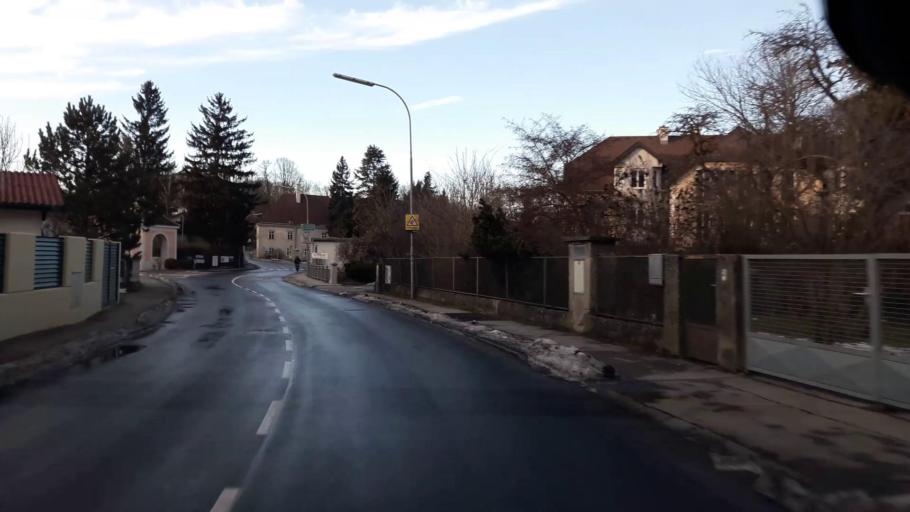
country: AT
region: Lower Austria
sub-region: Politischer Bezirk Wien-Umgebung
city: Mauerbach
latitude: 48.2450
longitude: 16.1685
